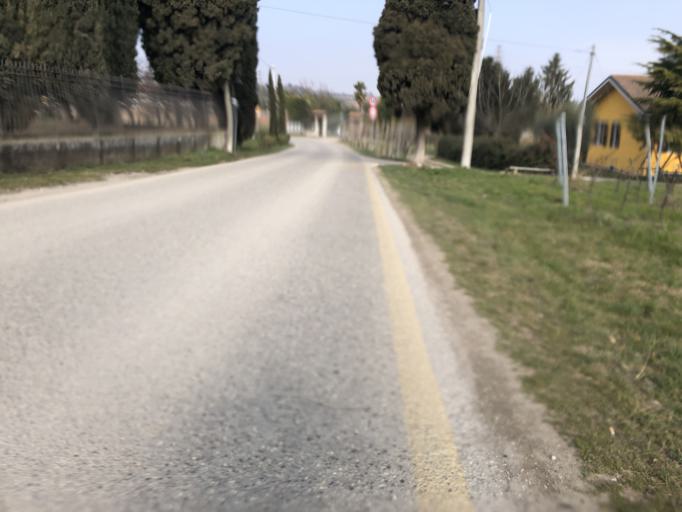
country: IT
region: Veneto
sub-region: Provincia di Verona
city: San Giorgio in Salici
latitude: 45.4186
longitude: 10.7989
